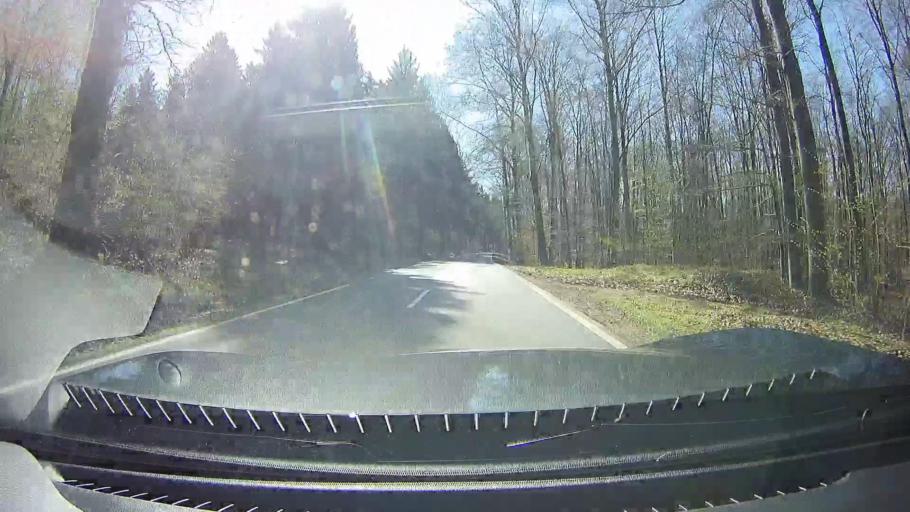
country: DE
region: Baden-Wuerttemberg
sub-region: Karlsruhe Region
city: Eberbach
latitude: 49.4253
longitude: 8.9786
